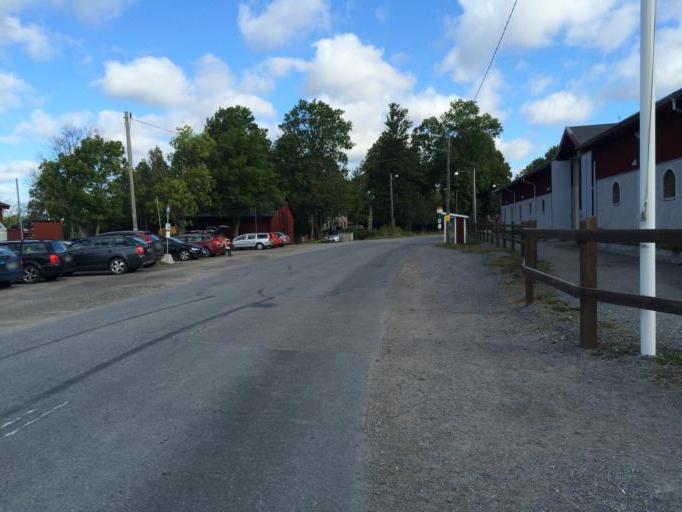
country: SE
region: Stockholm
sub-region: Haninge Kommun
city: Handen
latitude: 59.2210
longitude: 18.0811
